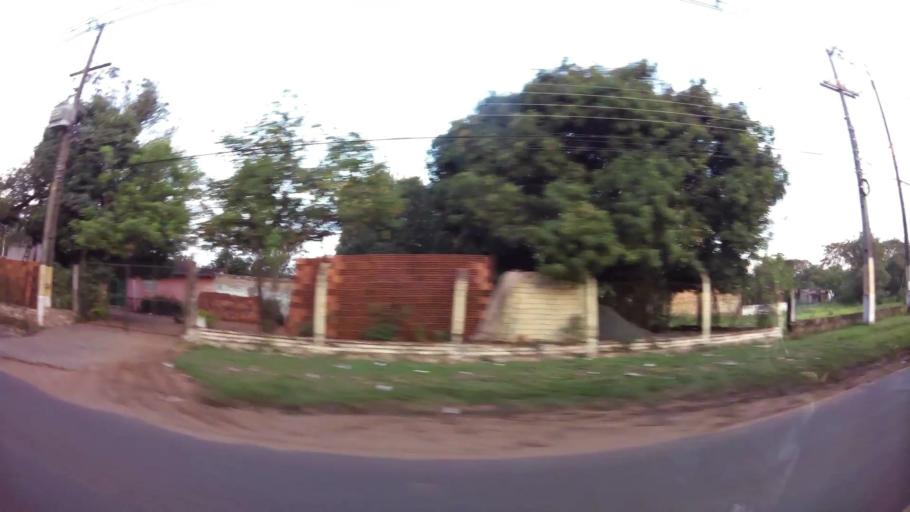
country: PY
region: Central
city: San Lorenzo
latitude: -25.3702
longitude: -57.4917
